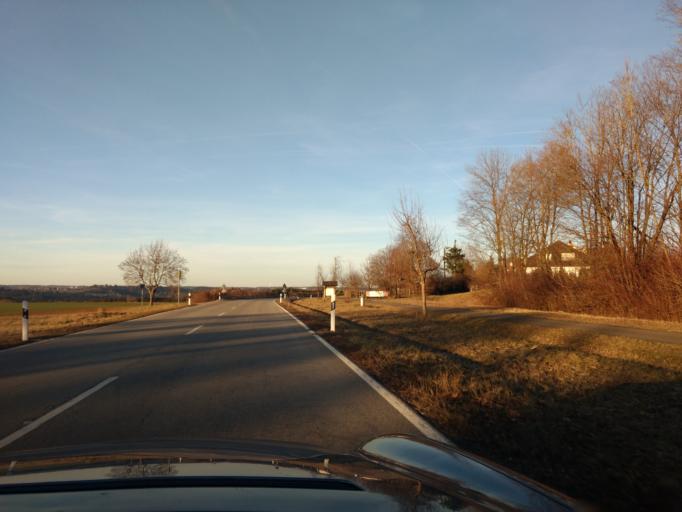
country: DE
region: Baden-Wuerttemberg
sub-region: Regierungsbezirk Stuttgart
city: Ottenbach
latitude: 48.7627
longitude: 9.7714
